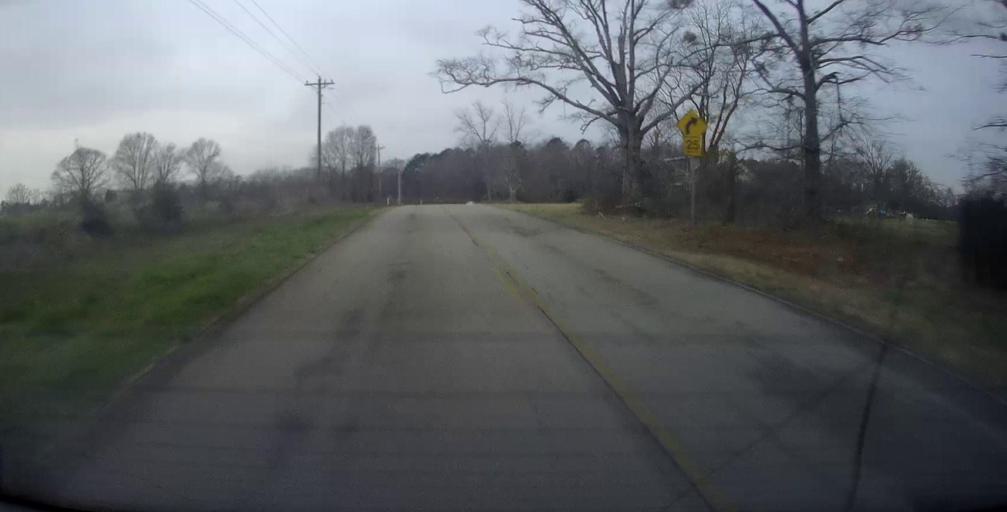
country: US
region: Georgia
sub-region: Monroe County
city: Forsyth
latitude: 32.9886
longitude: -84.0404
